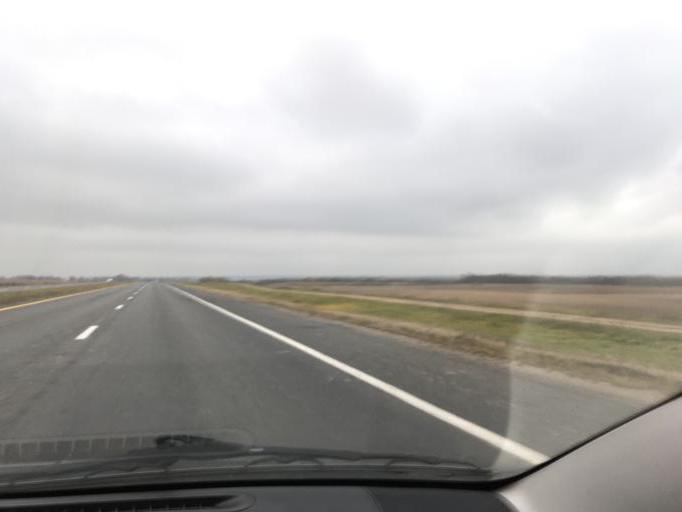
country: BY
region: Vitebsk
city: Vitebsk
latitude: 55.1556
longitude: 30.0842
